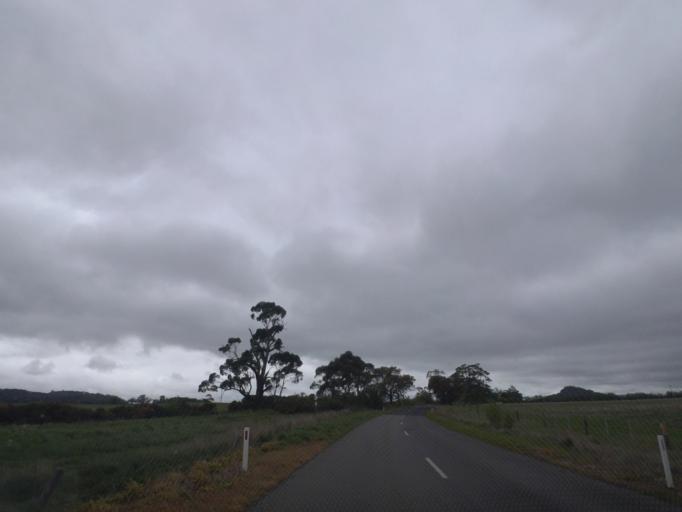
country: AU
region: Victoria
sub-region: Hume
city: Sunbury
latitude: -37.3241
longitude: 144.5616
